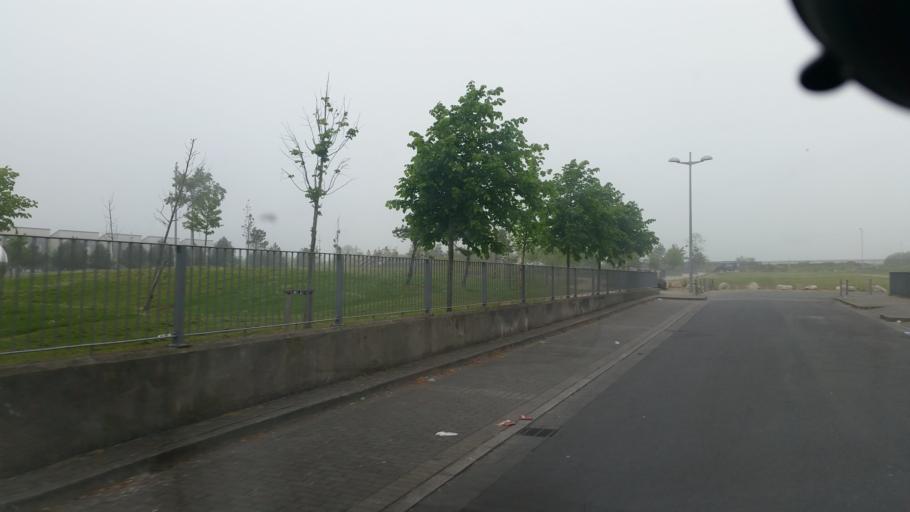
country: IE
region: Leinster
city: Ballymun
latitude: 53.3997
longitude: -6.2673
